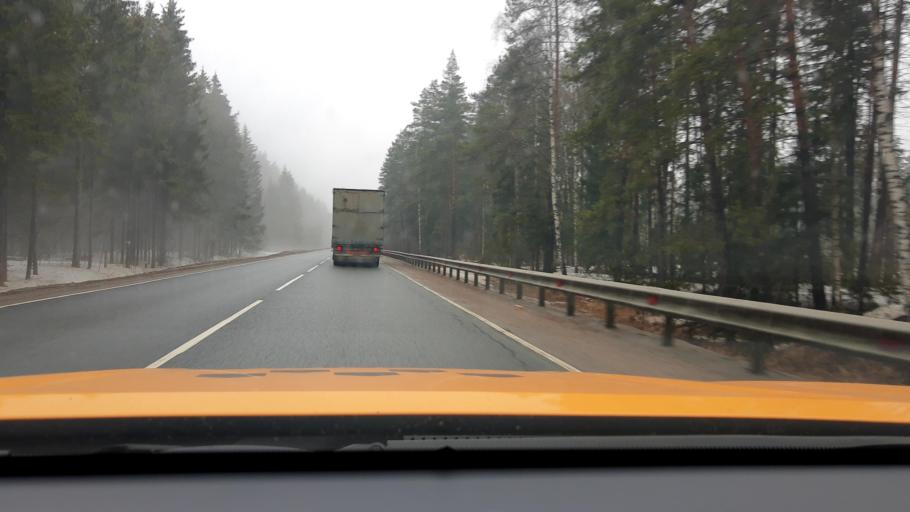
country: RU
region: Moskovskaya
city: Chernogolovka
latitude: 56.0128
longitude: 38.2639
